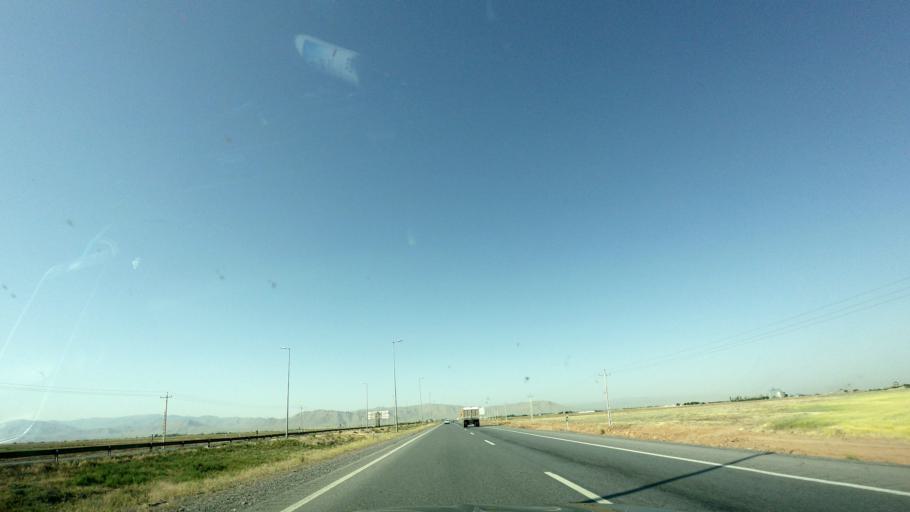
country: IR
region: Markazi
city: Ashtian
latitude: 34.1971
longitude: 50.0587
